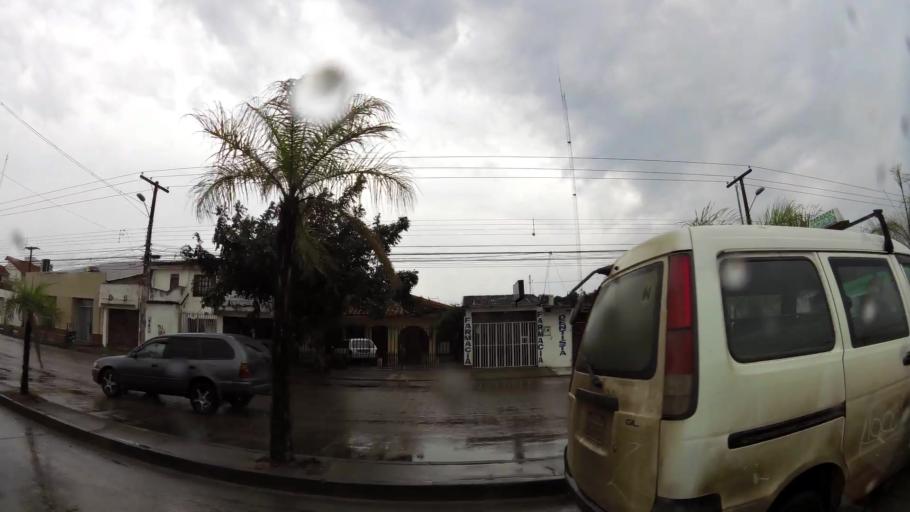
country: BO
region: Santa Cruz
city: Santa Cruz de la Sierra
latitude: -17.7597
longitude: -63.1572
